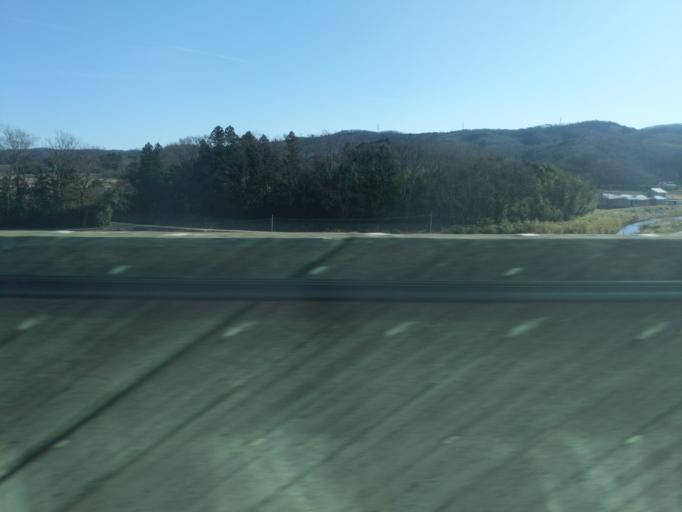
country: JP
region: Miyagi
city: Shiroishi
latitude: 37.9833
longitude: 140.6229
